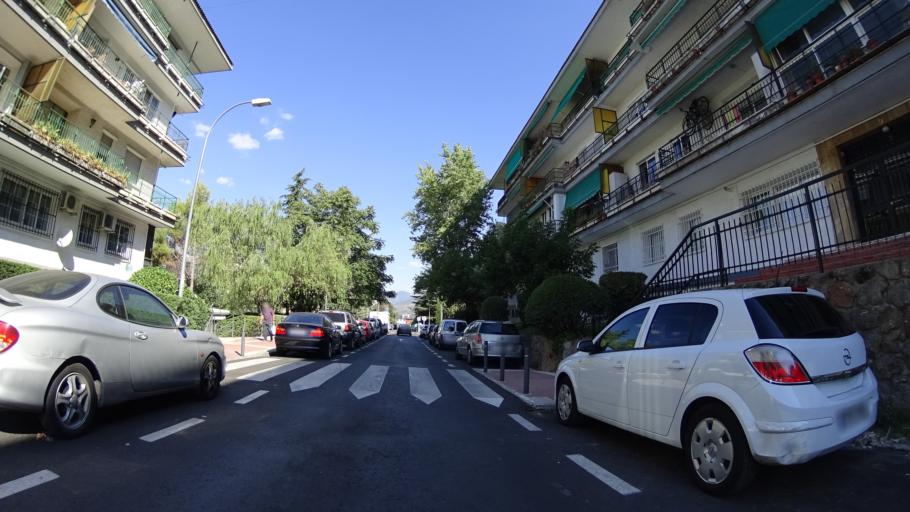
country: ES
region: Madrid
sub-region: Provincia de Madrid
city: Collado-Villalba
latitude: 40.6210
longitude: -4.0115
